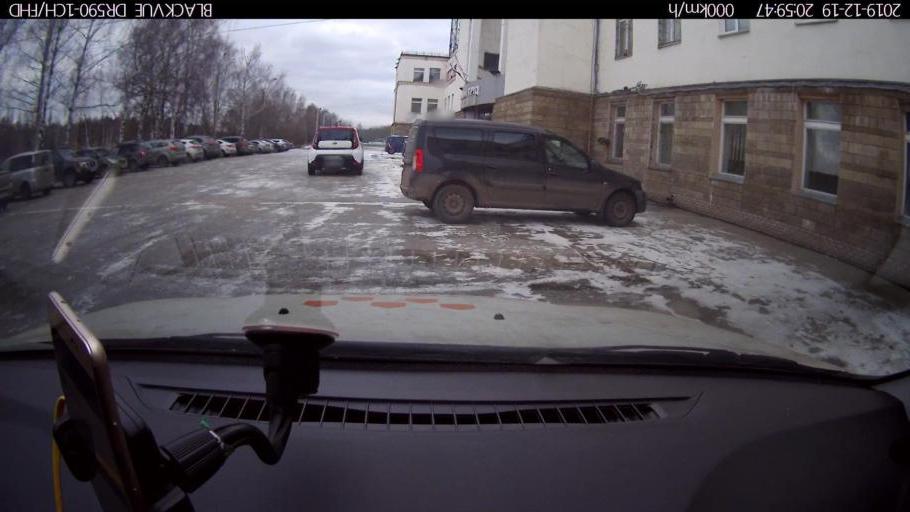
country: RU
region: Nizjnij Novgorod
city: Gorbatovka
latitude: 56.3432
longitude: 43.8553
